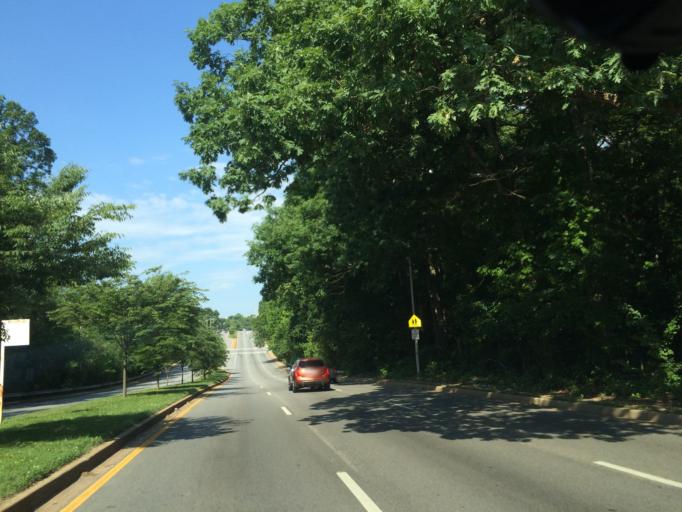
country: US
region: Maryland
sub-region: Baltimore County
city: Parkville
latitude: 39.3678
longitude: -76.5787
